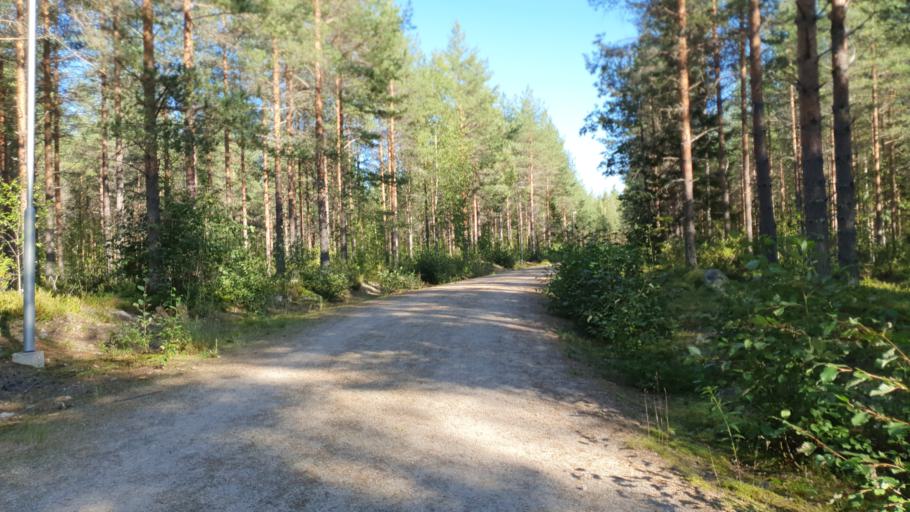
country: FI
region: Kainuu
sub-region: Kehys-Kainuu
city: Kuhmo
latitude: 64.1131
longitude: 29.5022
